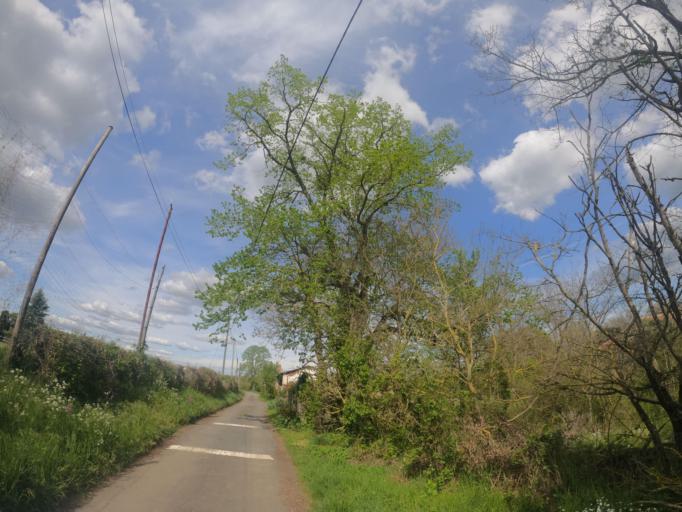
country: FR
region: Poitou-Charentes
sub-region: Departement des Deux-Sevres
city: Saint-Jean-de-Thouars
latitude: 46.9191
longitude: -0.1916
